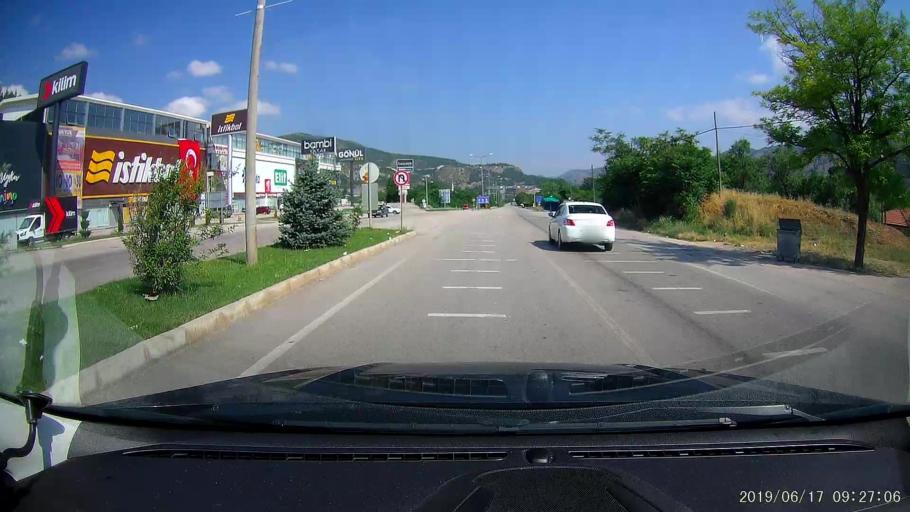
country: TR
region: Amasya
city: Amasya
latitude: 40.6738
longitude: 35.8291
